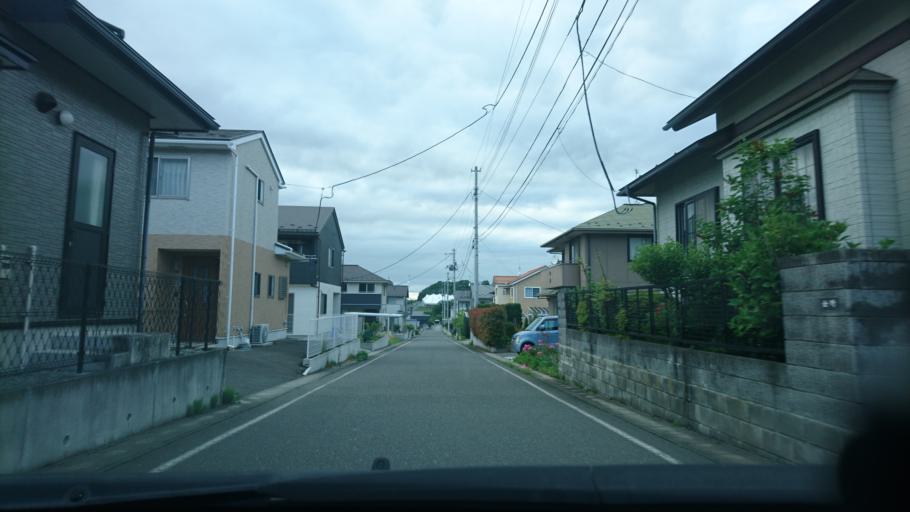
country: JP
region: Iwate
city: Ichinoseki
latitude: 38.9098
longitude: 141.1622
